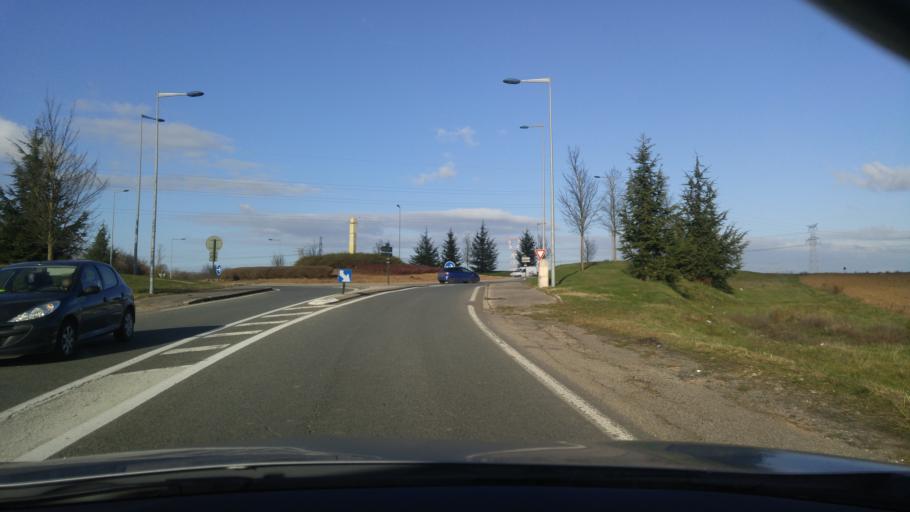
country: FR
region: Rhone-Alpes
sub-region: Departement de l'Isere
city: La Verpilliere
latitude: 45.6605
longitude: 5.1329
